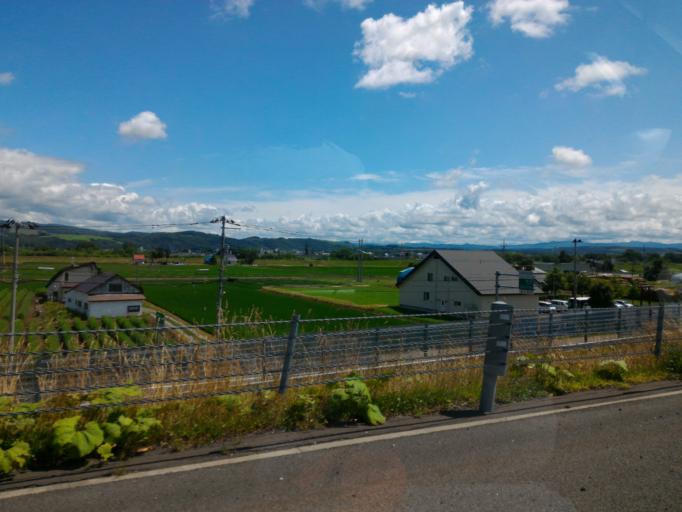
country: JP
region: Hokkaido
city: Nayoro
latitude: 44.3638
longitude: 142.4358
